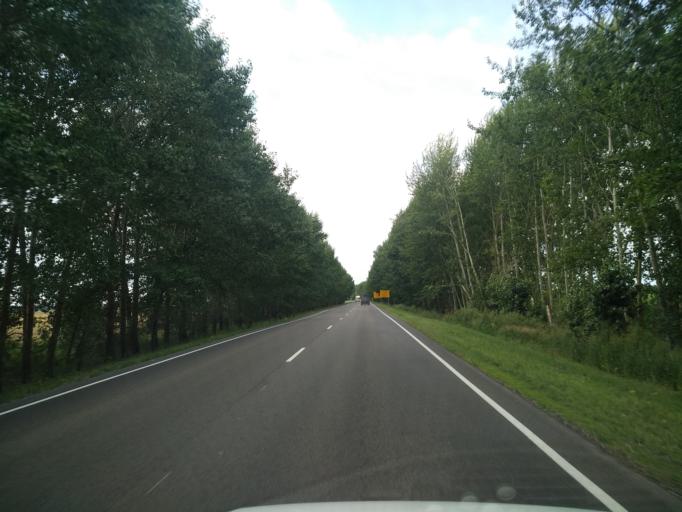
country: RU
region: Voronezj
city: Pereleshino
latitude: 51.8027
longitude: 40.1676
